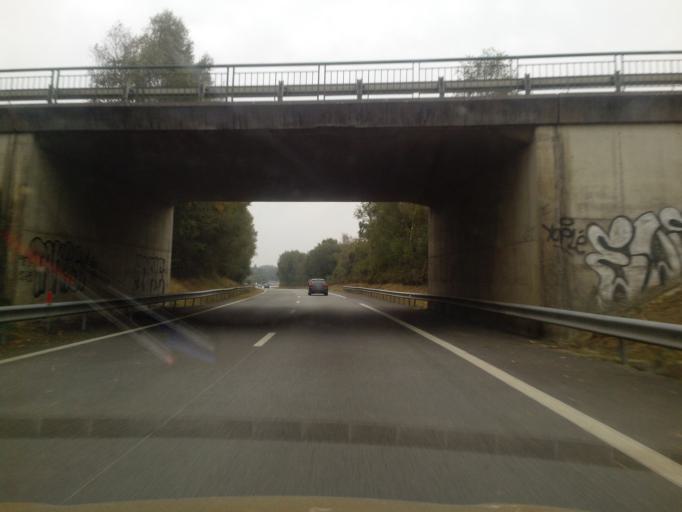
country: FR
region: Brittany
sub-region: Departement du Morbihan
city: Locmine
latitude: 47.8984
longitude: -2.8389
